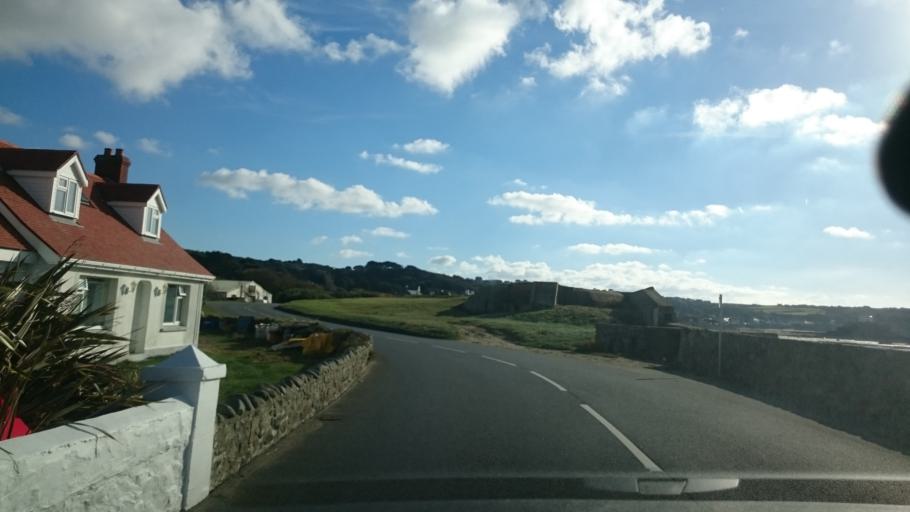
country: GG
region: St Peter Port
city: Saint Peter Port
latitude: 49.4451
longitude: -2.6492
